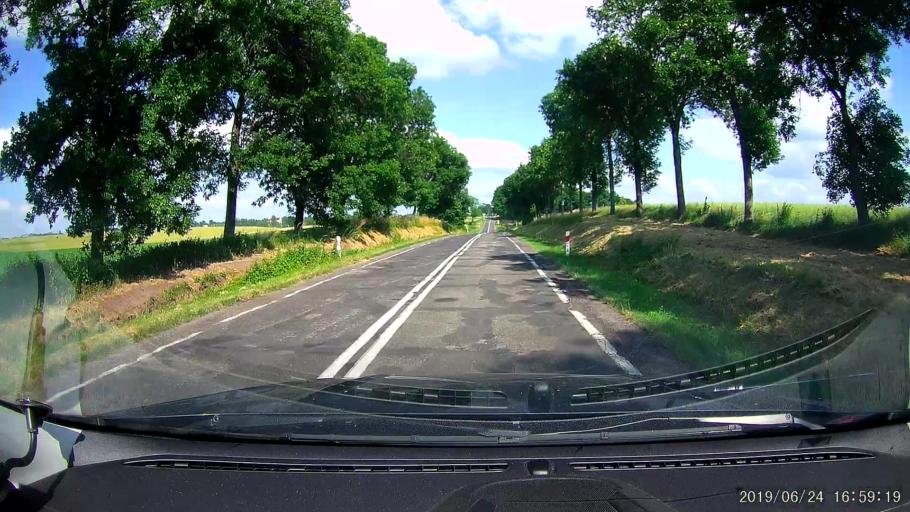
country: PL
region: Lublin Voivodeship
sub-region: Powiat tomaszowski
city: Telatyn
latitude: 50.5238
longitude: 23.8993
